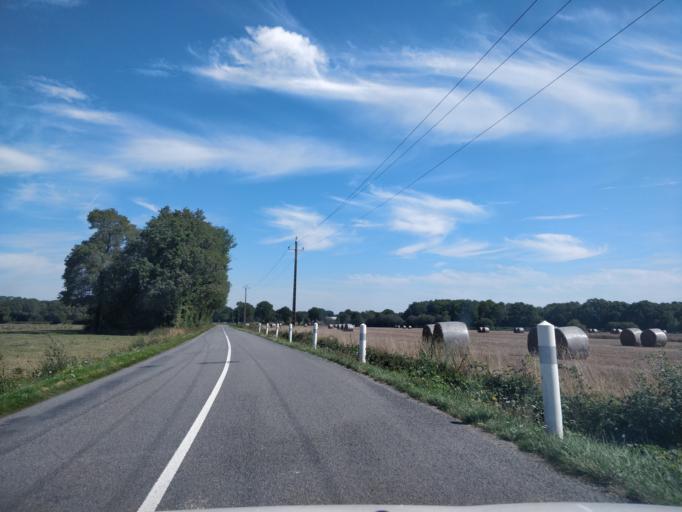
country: FR
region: Pays de la Loire
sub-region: Departement de la Loire-Atlantique
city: Conquereuil
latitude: 47.6573
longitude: -1.7831
